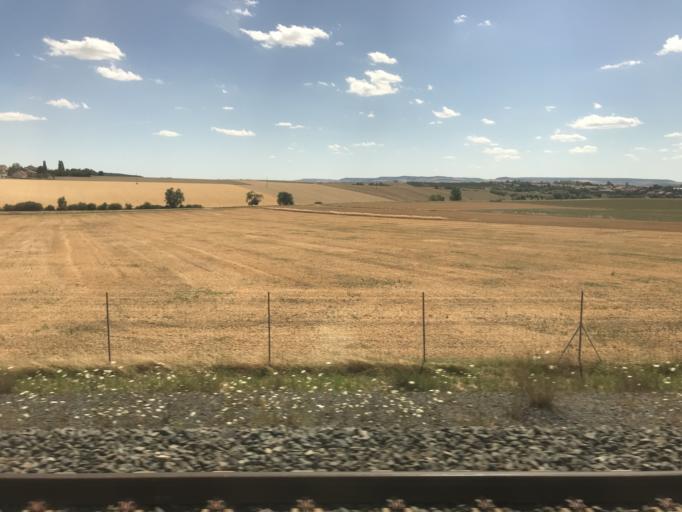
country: FR
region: Lorraine
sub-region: Departement de la Moselle
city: Verny
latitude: 48.9577
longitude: 6.2251
